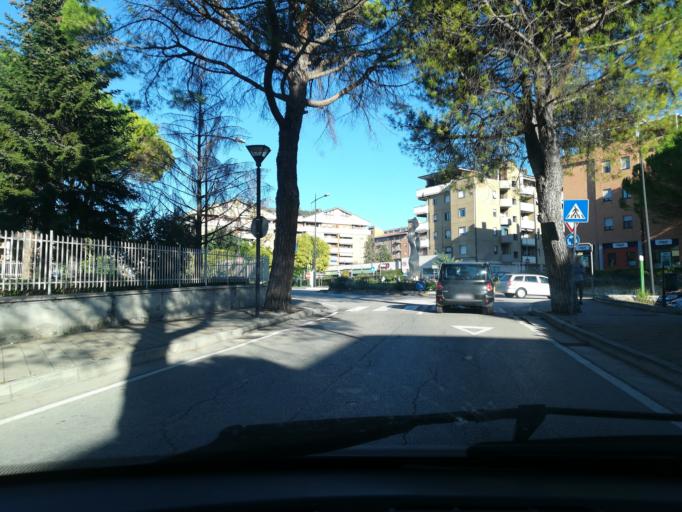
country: IT
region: The Marches
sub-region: Provincia di Macerata
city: Tolentino
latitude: 43.2123
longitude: 13.2933
